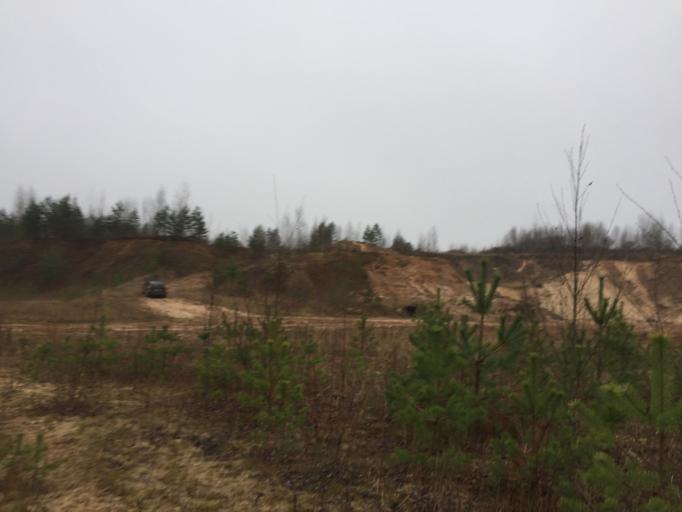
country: LV
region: Koceni
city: Koceni
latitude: 57.5188
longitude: 25.2980
